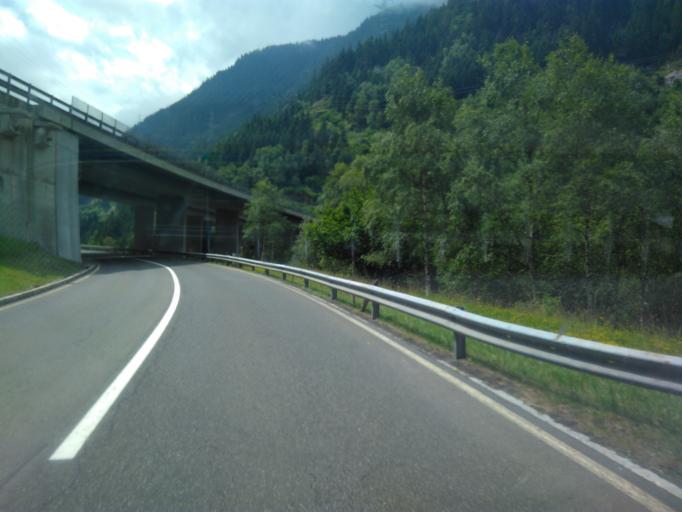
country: CH
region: Uri
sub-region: Uri
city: Andermatt
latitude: 46.6882
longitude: 8.5938
